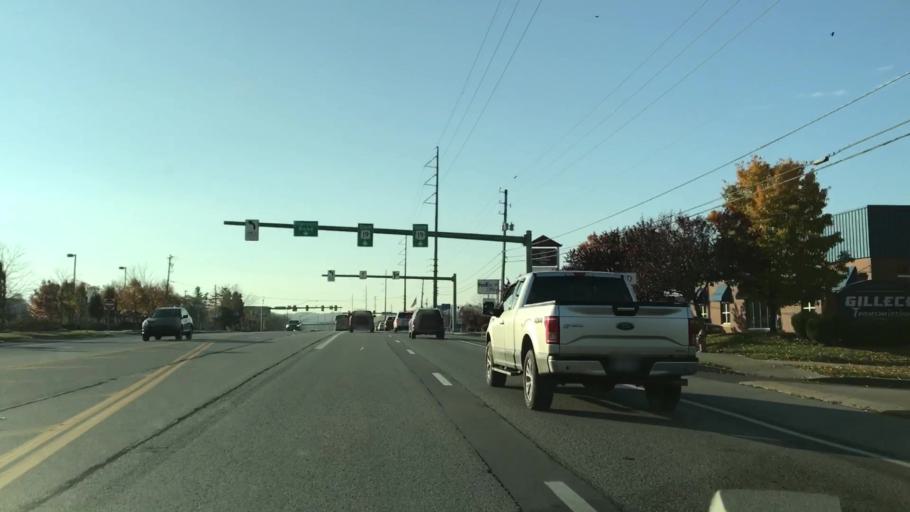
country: US
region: Pennsylvania
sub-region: Butler County
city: Cranberry Township
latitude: 40.6753
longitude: -80.0990
